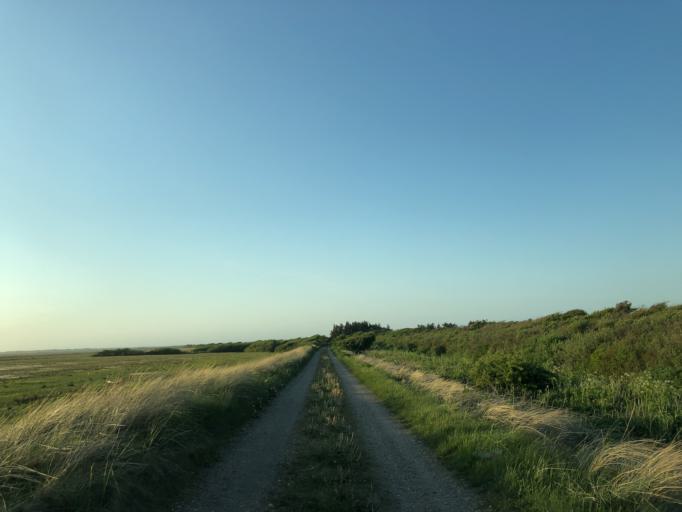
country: DK
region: Central Jutland
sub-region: Ringkobing-Skjern Kommune
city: Ringkobing
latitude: 56.2255
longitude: 8.1669
